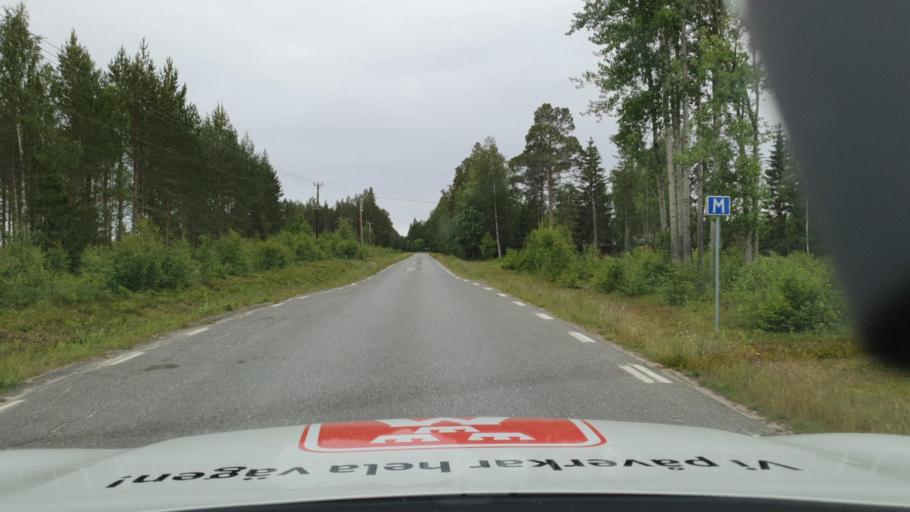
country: SE
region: Vaesterbotten
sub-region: Nordmalings Kommun
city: Nordmaling
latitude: 63.4396
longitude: 19.4691
